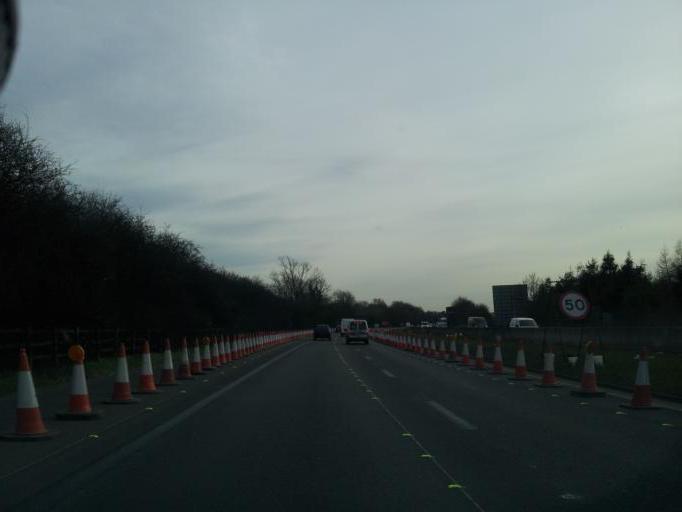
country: GB
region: England
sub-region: Hertfordshire
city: Hatfield
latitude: 51.7236
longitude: -0.2237
